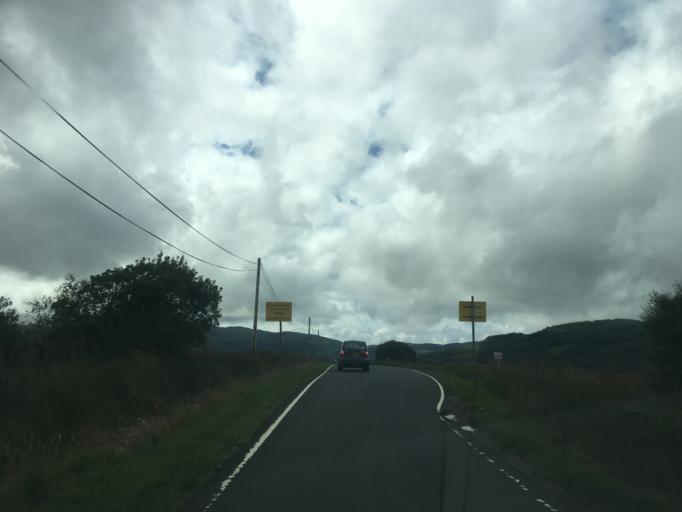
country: GB
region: Scotland
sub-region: Argyll and Bute
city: Port Bannatyne
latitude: 55.9911
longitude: -5.1411
